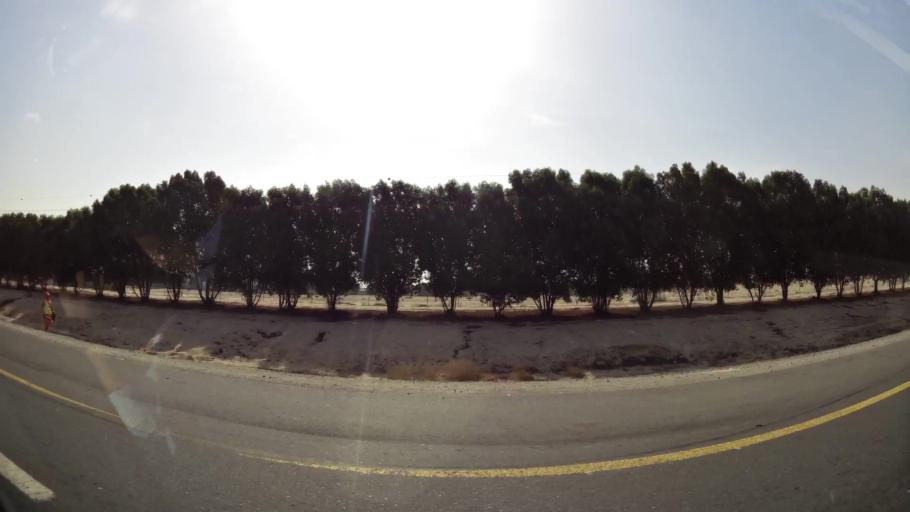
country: AE
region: Ash Shariqah
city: Sharjah
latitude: 25.2434
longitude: 55.4050
